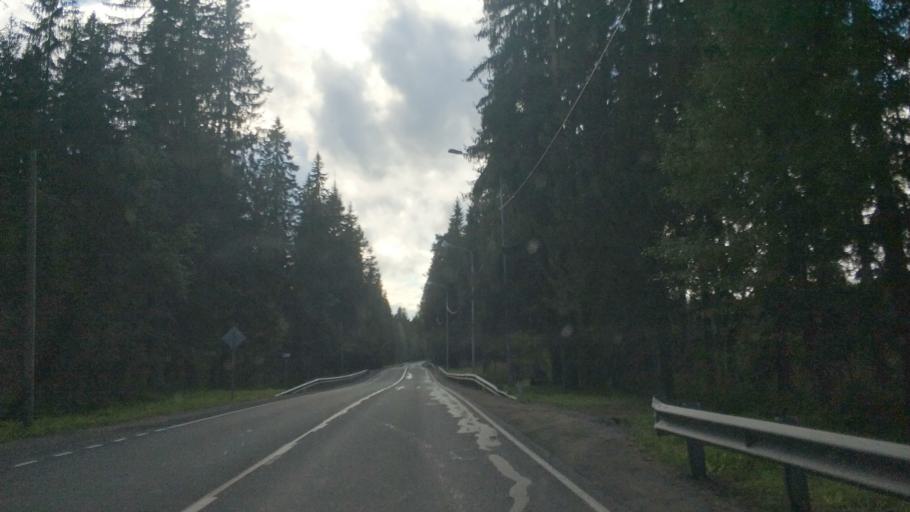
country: RU
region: Republic of Karelia
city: Lakhdenpokh'ya
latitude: 61.5153
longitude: 30.1277
